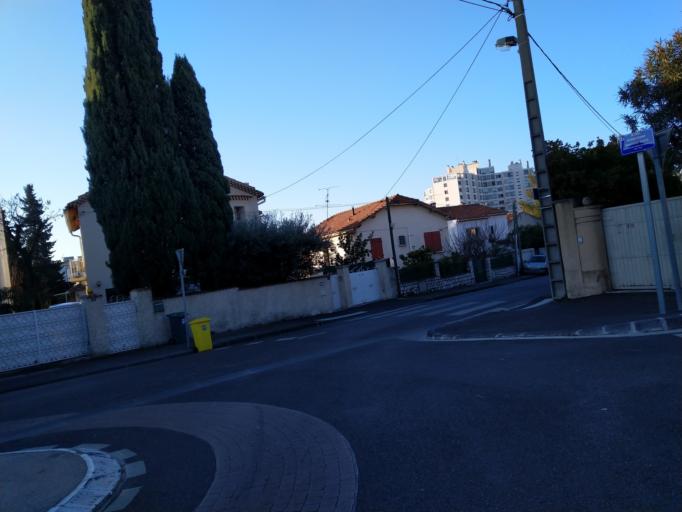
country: FR
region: Provence-Alpes-Cote d'Azur
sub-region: Departement des Bouches-du-Rhone
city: Marseille 12
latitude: 43.3045
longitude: 5.4318
